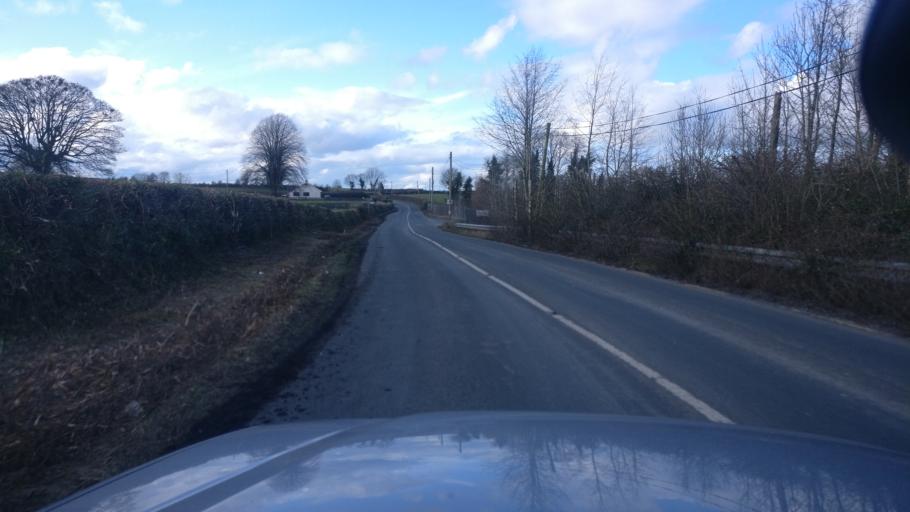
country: IE
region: Connaught
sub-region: County Galway
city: Portumna
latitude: 53.1644
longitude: -8.3861
